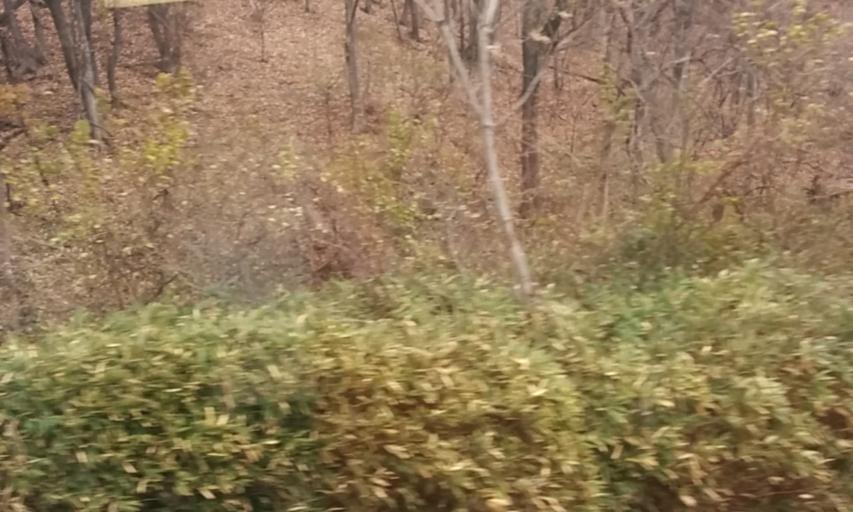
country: JP
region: Nagano
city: Nagano-shi
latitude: 36.4971
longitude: 138.1511
